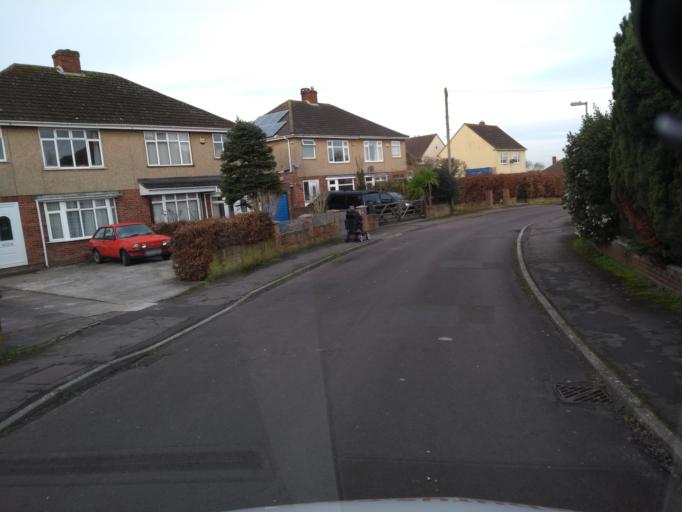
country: GB
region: England
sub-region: Somerset
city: Street
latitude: 51.1217
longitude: -2.7482
